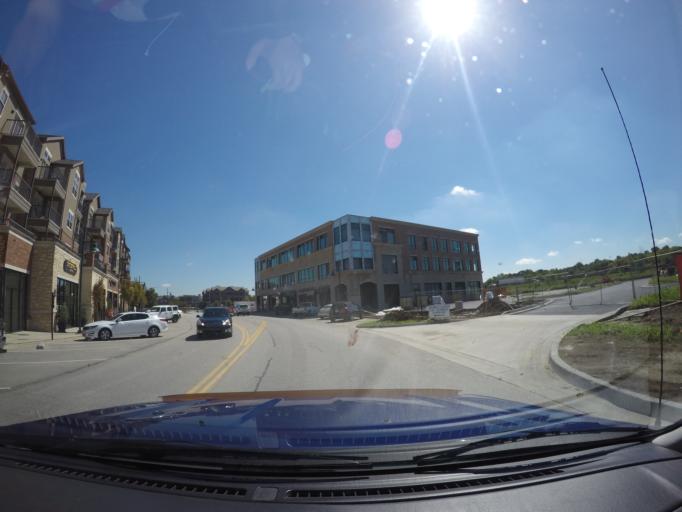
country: US
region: Kansas
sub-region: Johnson County
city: Leawood
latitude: 38.9345
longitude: -94.6322
